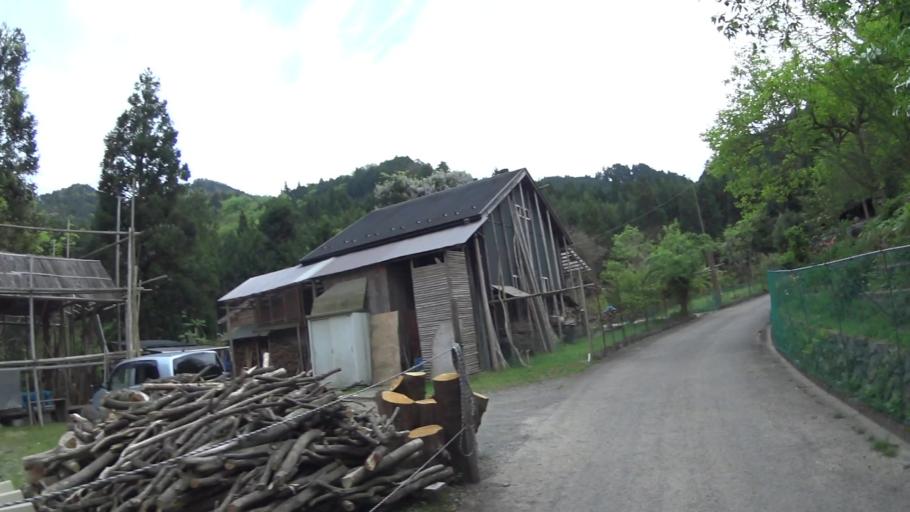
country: JP
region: Kyoto
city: Kameoka
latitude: 35.1108
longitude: 135.6329
